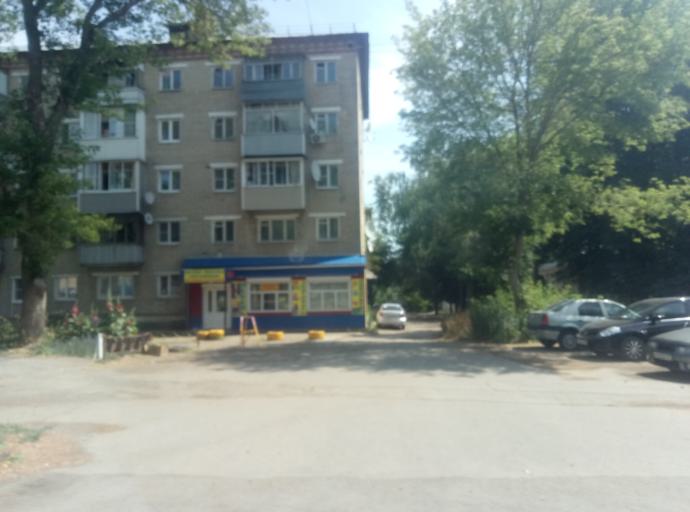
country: RU
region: Tula
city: Kireyevsk
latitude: 53.9261
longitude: 37.9350
